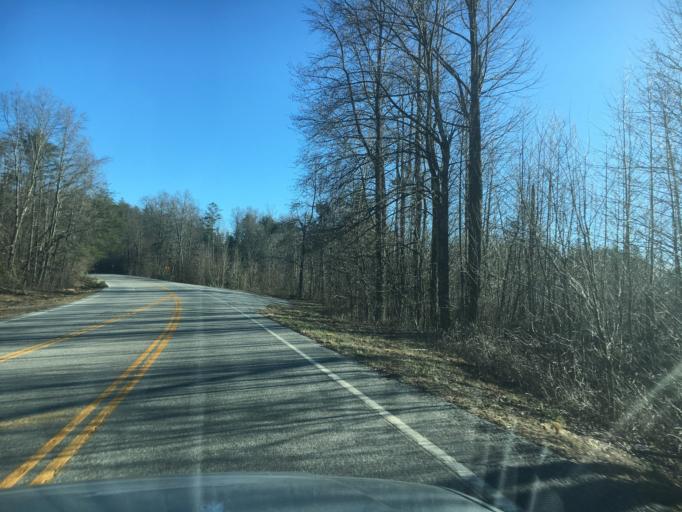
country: US
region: Georgia
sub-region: White County
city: Cleveland
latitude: 34.6880
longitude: -83.9079
